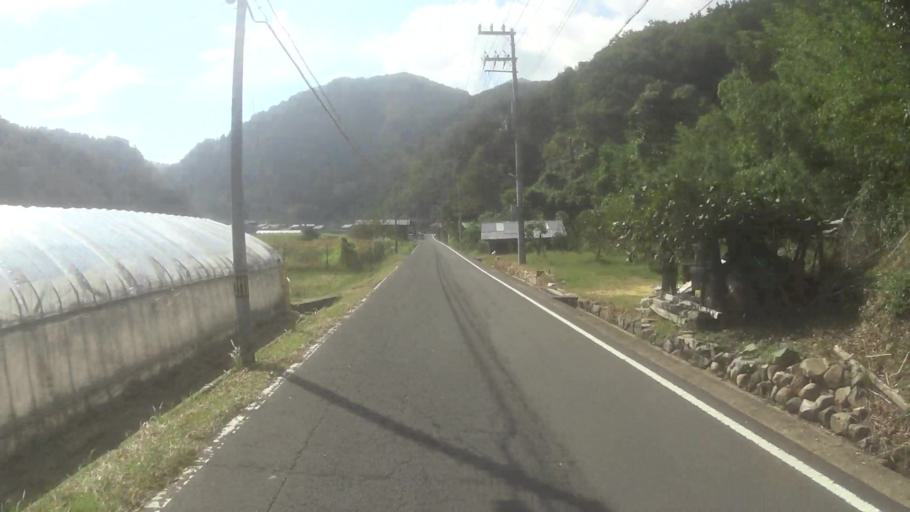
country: JP
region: Kyoto
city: Miyazu
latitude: 35.7388
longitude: 135.1574
